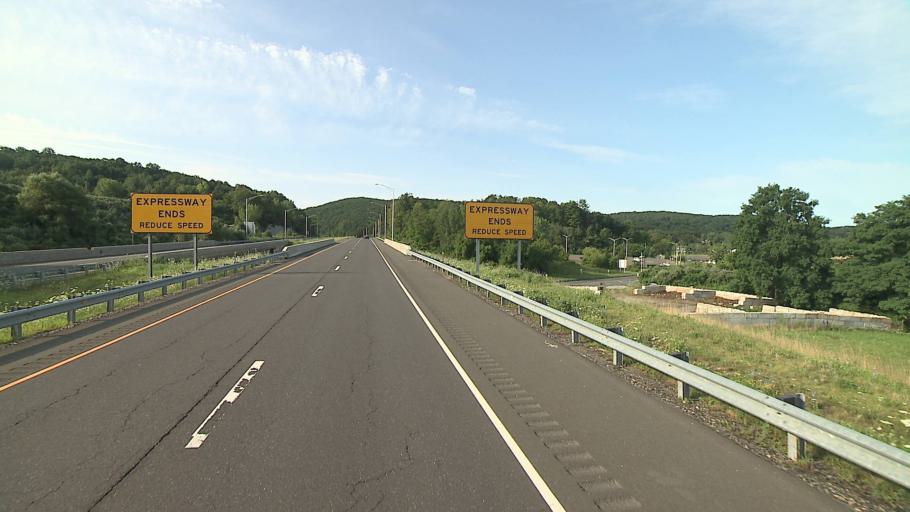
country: US
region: Connecticut
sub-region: Fairfield County
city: Danbury
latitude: 41.3720
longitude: -73.4738
